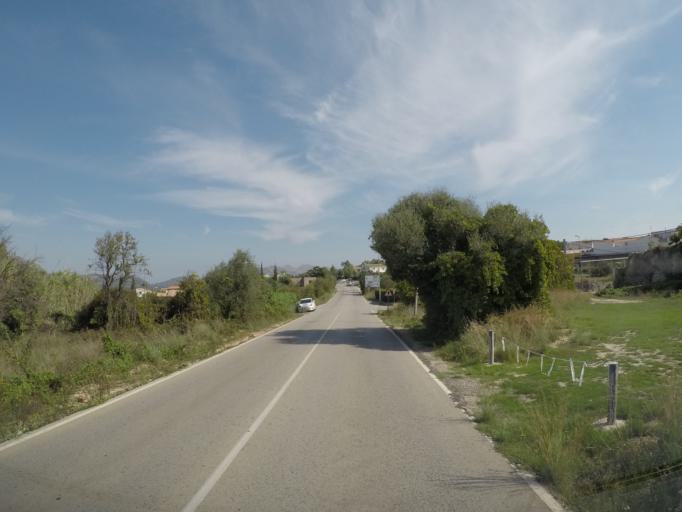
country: ES
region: Valencia
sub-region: Provincia de Alicante
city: Orba
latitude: 38.7816
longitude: -0.0649
